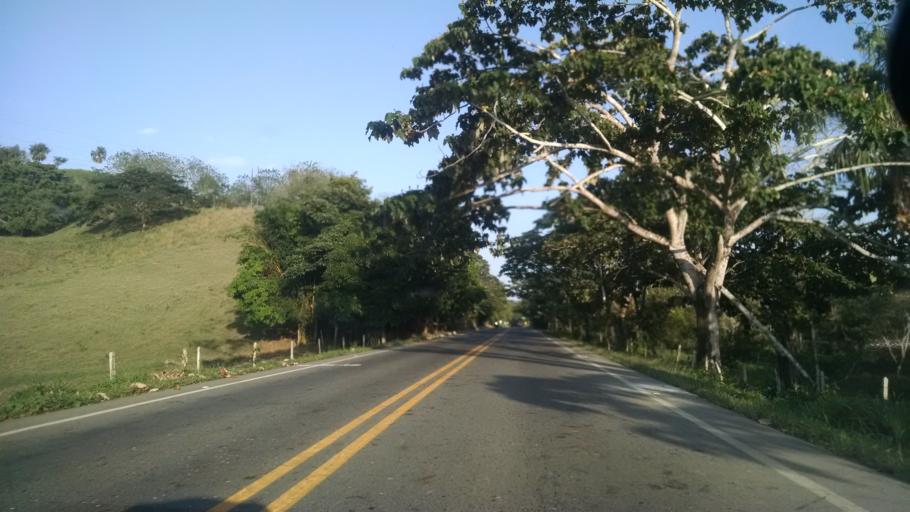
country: CO
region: Cordoba
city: Canalete
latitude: 8.8466
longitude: -76.1450
